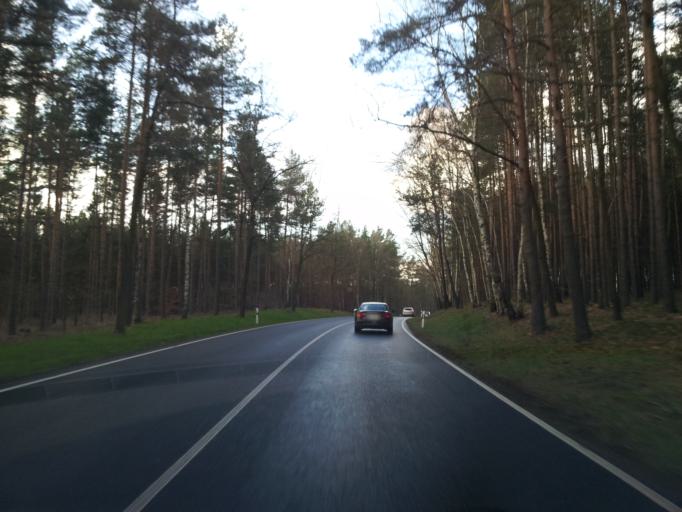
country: DE
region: Saxony
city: Konigsbruck
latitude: 51.2747
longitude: 13.9073
